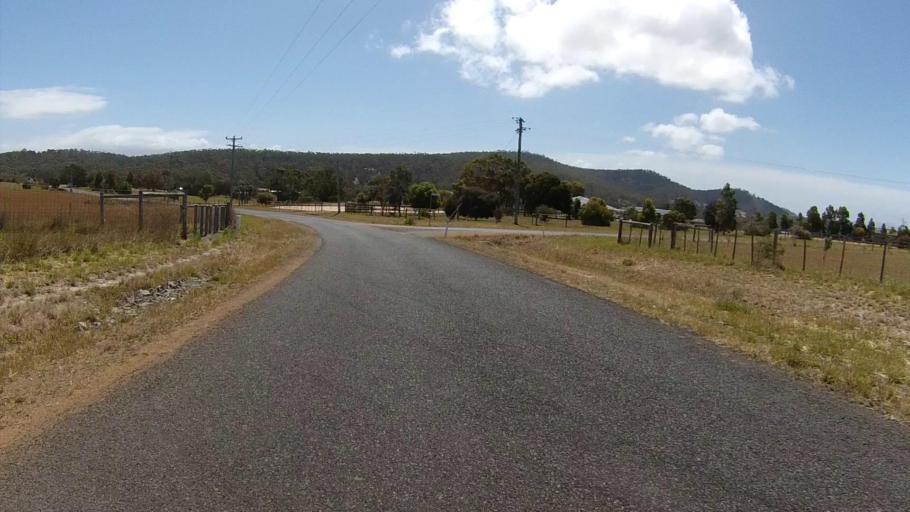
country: AU
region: Tasmania
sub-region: Clarence
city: Sandford
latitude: -42.9573
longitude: 147.4826
